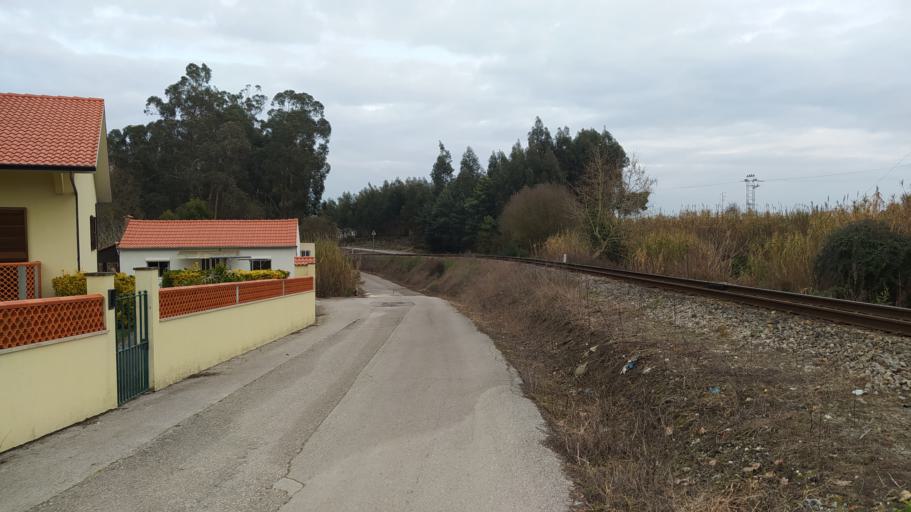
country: PT
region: Aveiro
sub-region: Aveiro
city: Eixo
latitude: 40.6399
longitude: -8.5914
